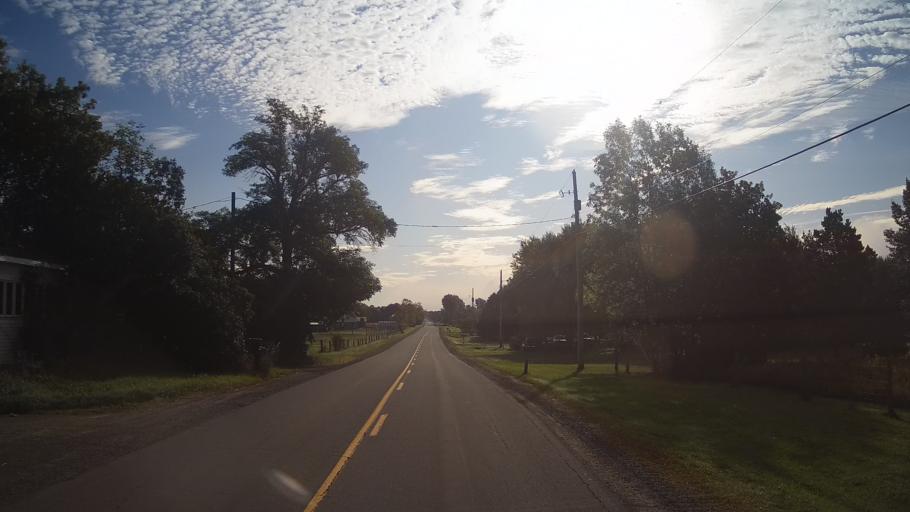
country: CA
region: Ontario
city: Gananoque
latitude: 44.4006
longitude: -76.0872
